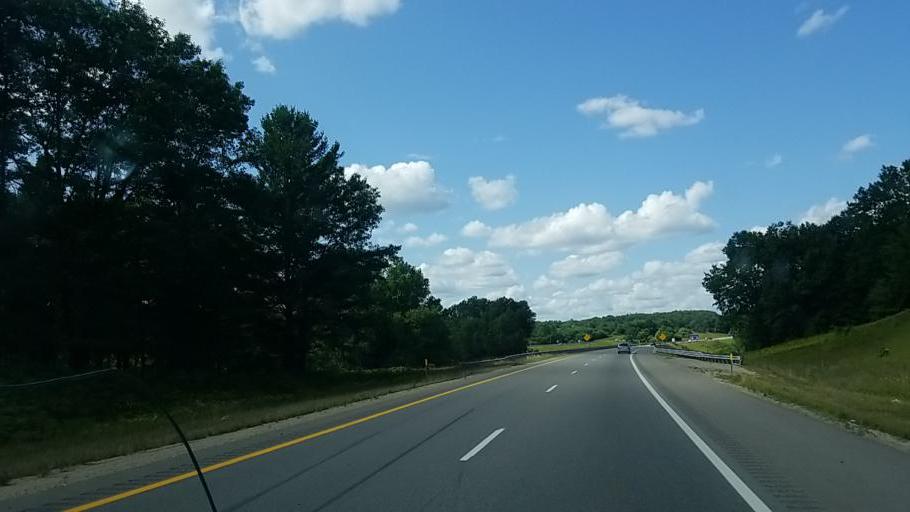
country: US
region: Michigan
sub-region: Mecosta County
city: Big Rapids
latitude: 43.6537
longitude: -85.5184
